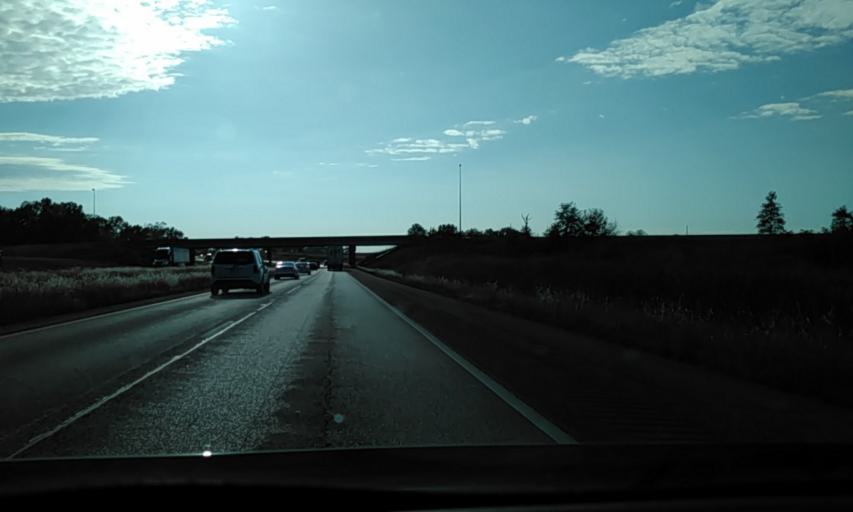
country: US
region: Illinois
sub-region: Bond County
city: Greenville
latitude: 38.8325
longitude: -89.5435
